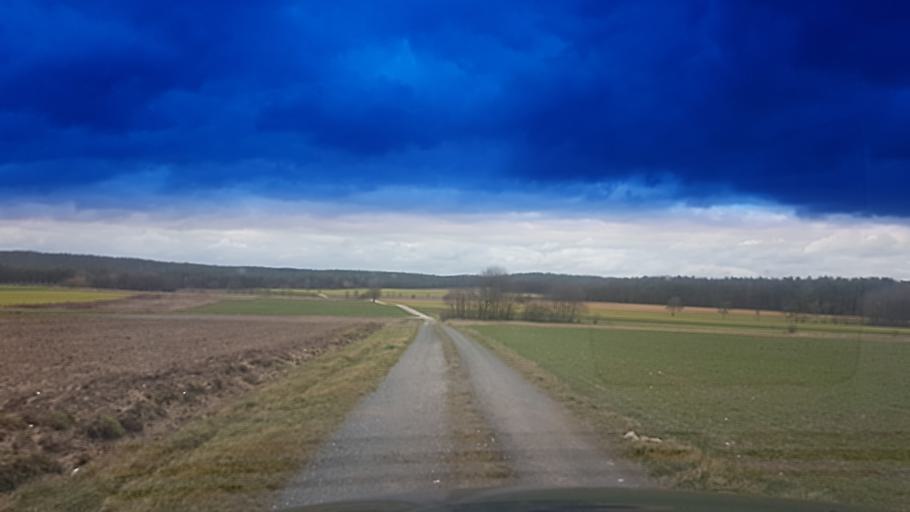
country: DE
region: Bavaria
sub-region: Upper Franconia
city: Lauter
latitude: 49.9460
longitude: 10.7734
